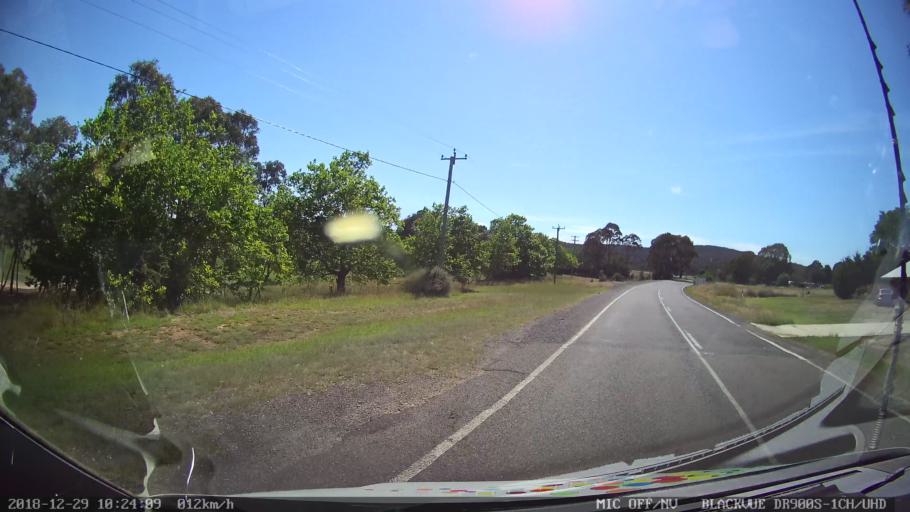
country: AU
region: New South Wales
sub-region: Yass Valley
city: Gundaroo
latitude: -34.9128
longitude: 149.4368
